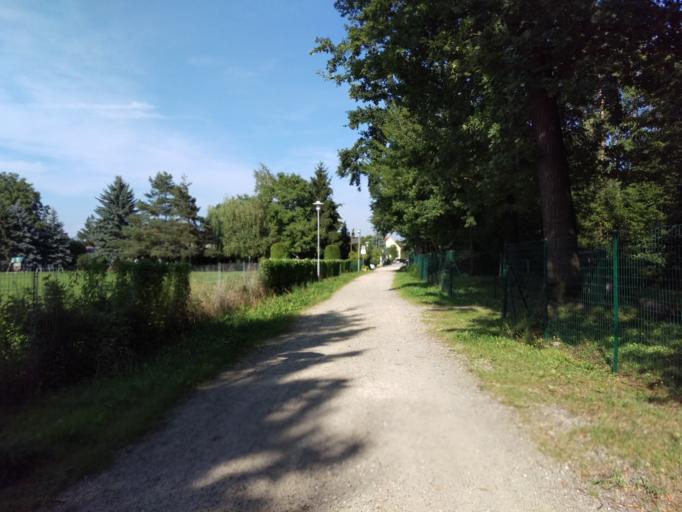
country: AT
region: Styria
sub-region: Politischer Bezirk Graz-Umgebung
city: Seiersberg
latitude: 47.0140
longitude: 15.4153
